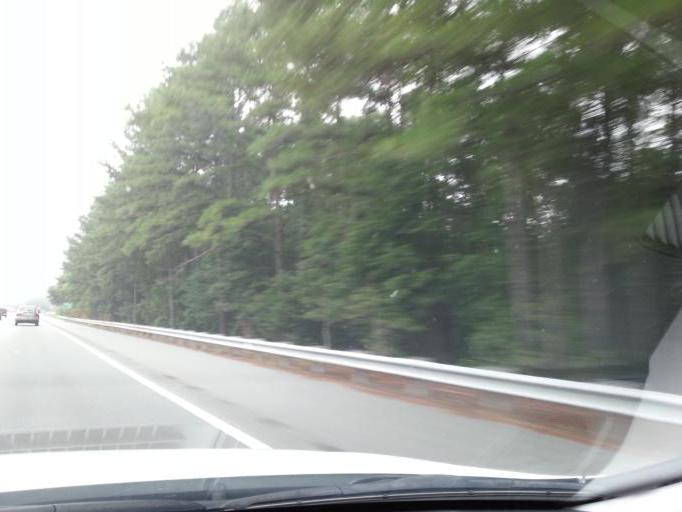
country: US
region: North Carolina
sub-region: Cumberland County
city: Fort Bragg
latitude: 35.0915
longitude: -78.9669
